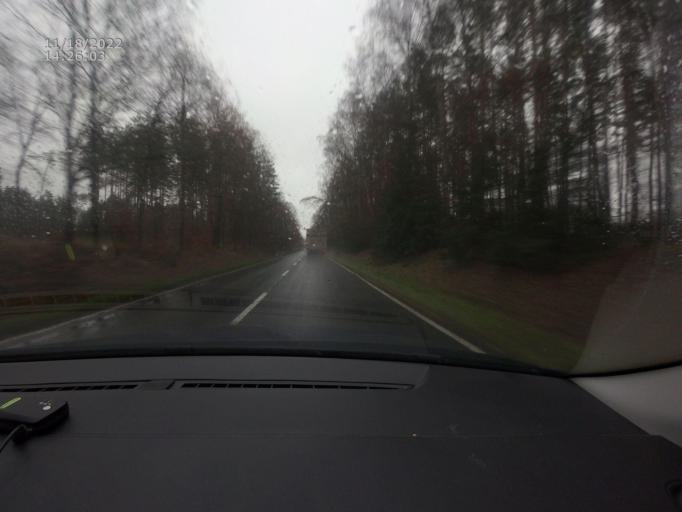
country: CZ
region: Jihocesky
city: Cimelice
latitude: 49.4326
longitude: 14.1653
